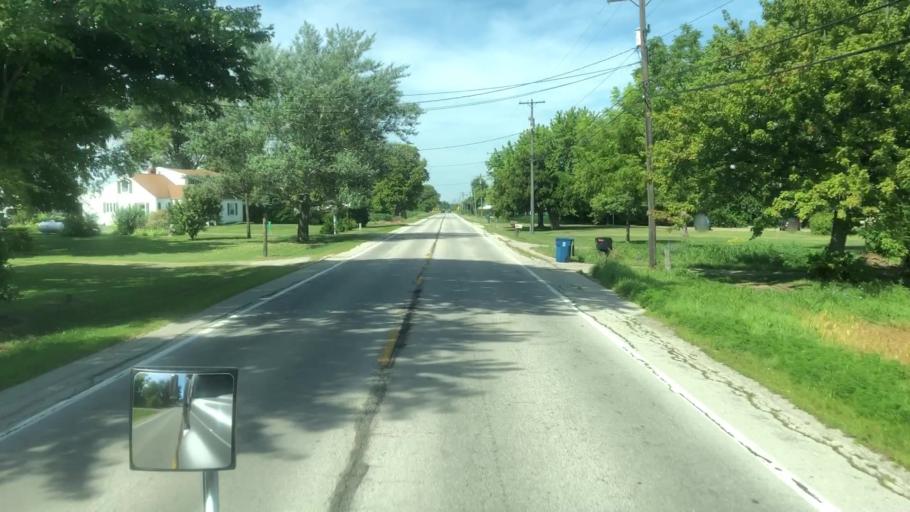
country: US
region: Ohio
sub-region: Ottawa County
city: Port Clinton
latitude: 41.4110
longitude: -82.9097
